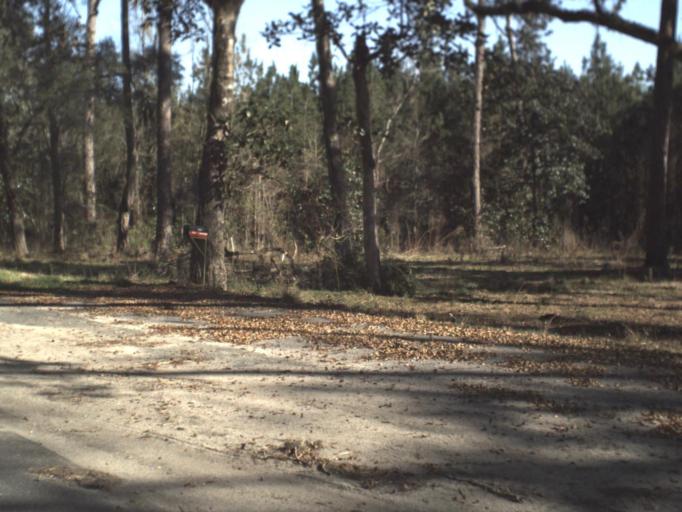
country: US
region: Florida
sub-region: Washington County
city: Chipley
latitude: 30.7920
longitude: -85.3844
